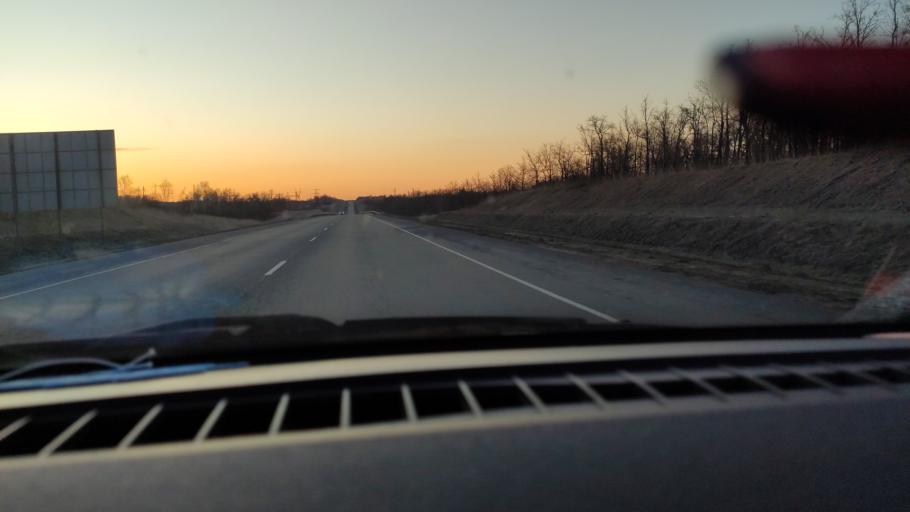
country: RU
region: Saratov
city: Yelshanka
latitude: 51.8241
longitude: 46.3071
